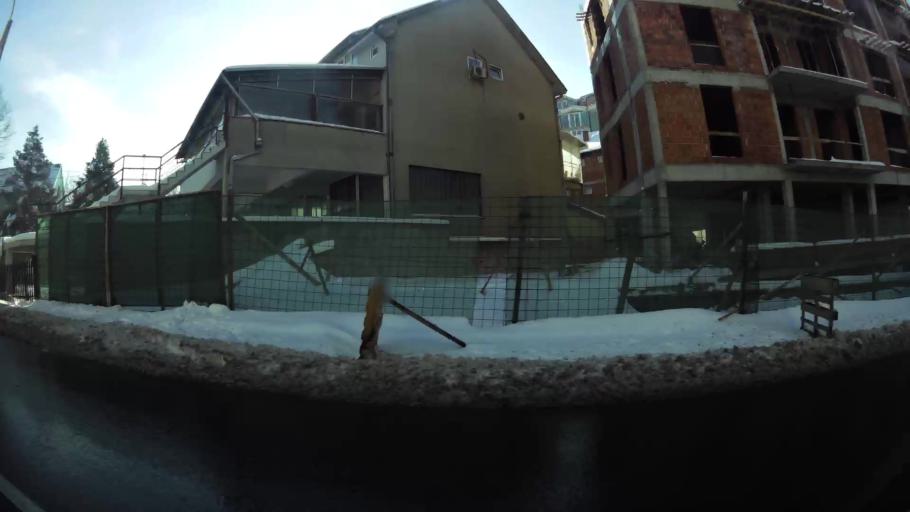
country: RS
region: Central Serbia
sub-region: Belgrade
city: Palilula
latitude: 44.8162
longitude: 20.5040
